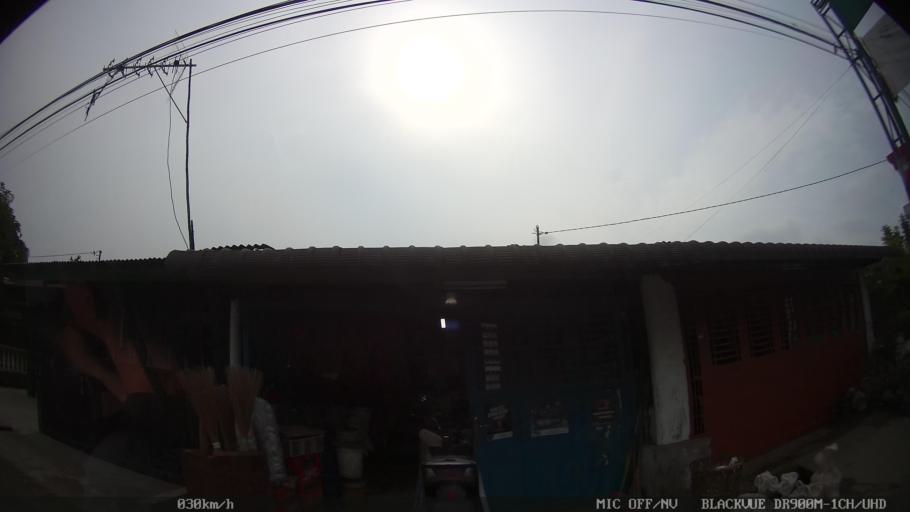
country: ID
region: North Sumatra
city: Medan
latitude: 3.5717
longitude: 98.7565
